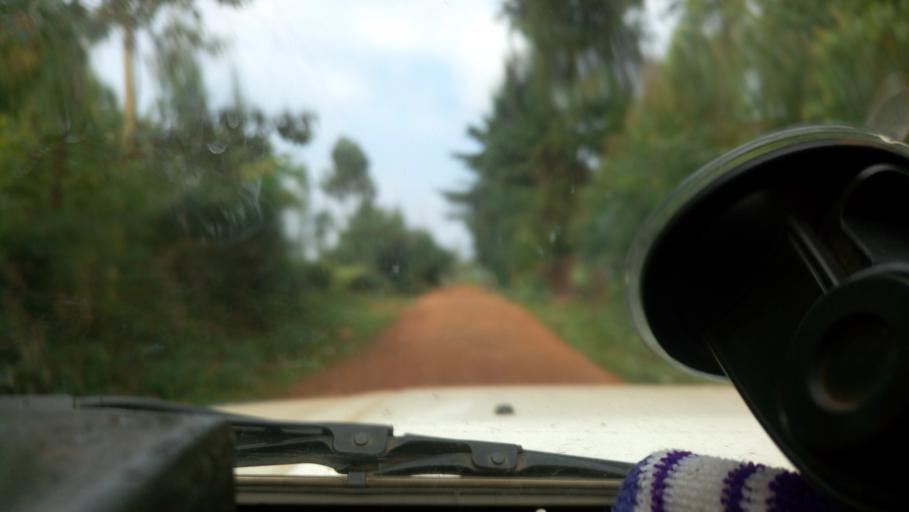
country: KE
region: Kericho
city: Litein
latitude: -0.5642
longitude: 35.2014
